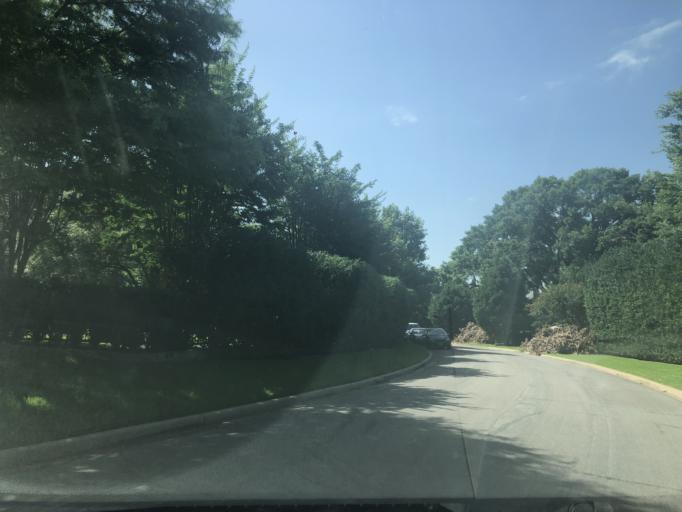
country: US
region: Texas
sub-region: Dallas County
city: University Park
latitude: 32.8852
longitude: -96.8174
